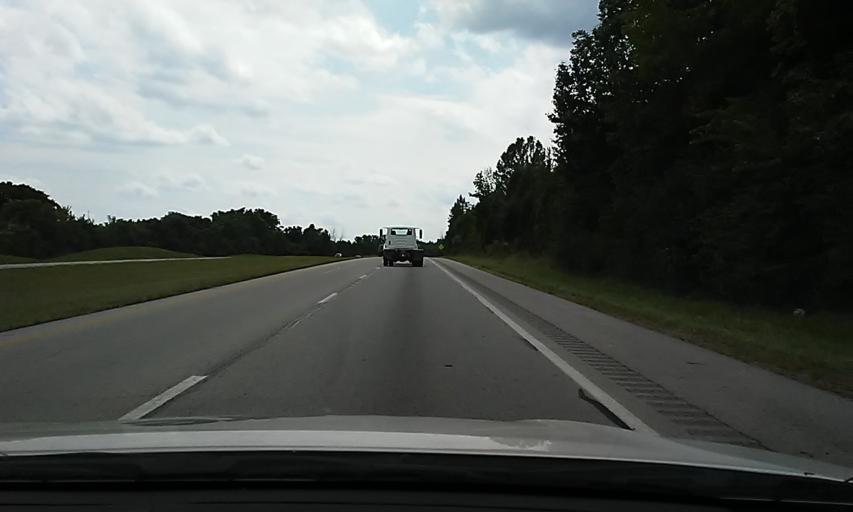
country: US
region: Ohio
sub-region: Greene County
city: Wright-Patterson AFB
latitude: 39.8320
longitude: -84.0625
